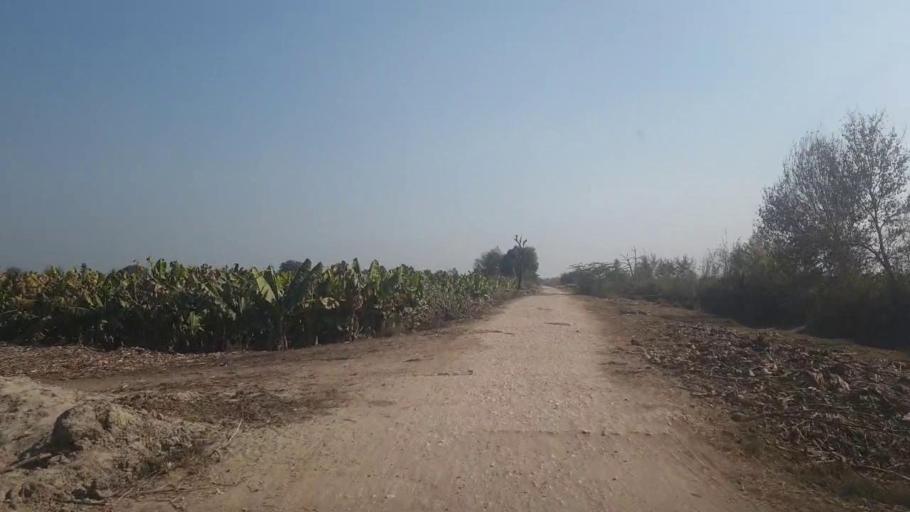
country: PK
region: Sindh
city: Sakrand
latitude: 26.0689
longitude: 68.4304
